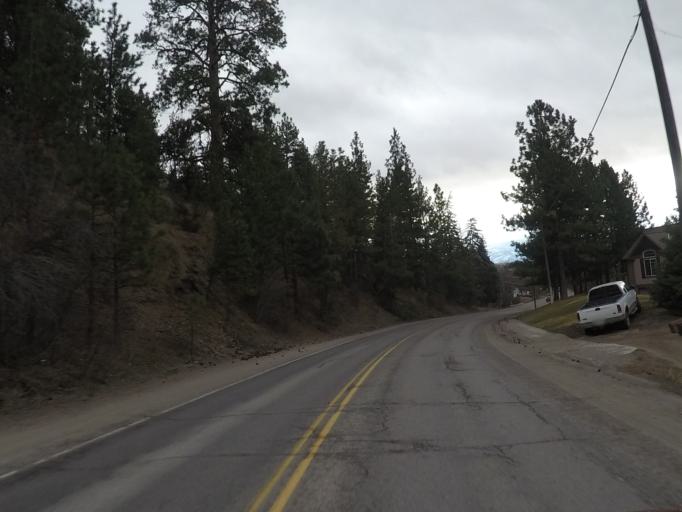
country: US
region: Montana
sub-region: Missoula County
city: Missoula
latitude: 46.8784
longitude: -113.9701
